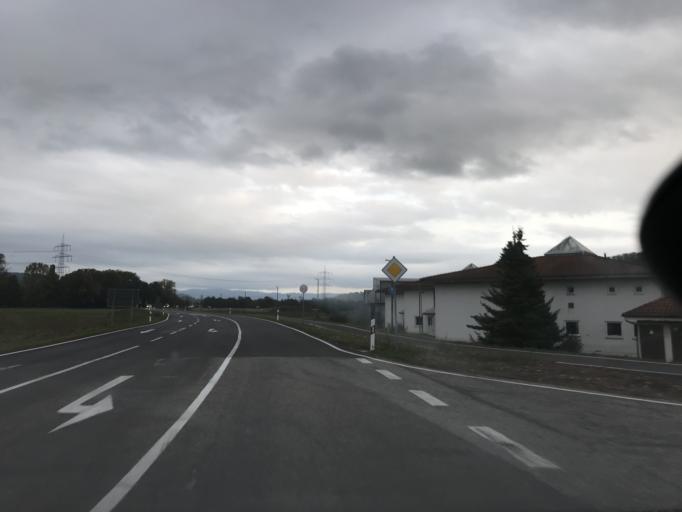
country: DE
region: Baden-Wuerttemberg
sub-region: Freiburg Region
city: Steinen
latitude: 47.6421
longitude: 7.7048
